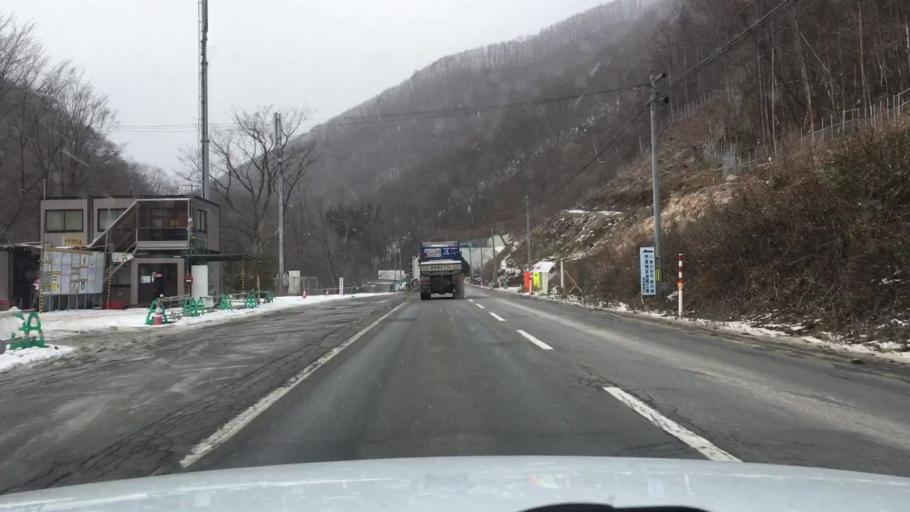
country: JP
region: Iwate
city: Tono
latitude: 39.6243
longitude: 141.4707
